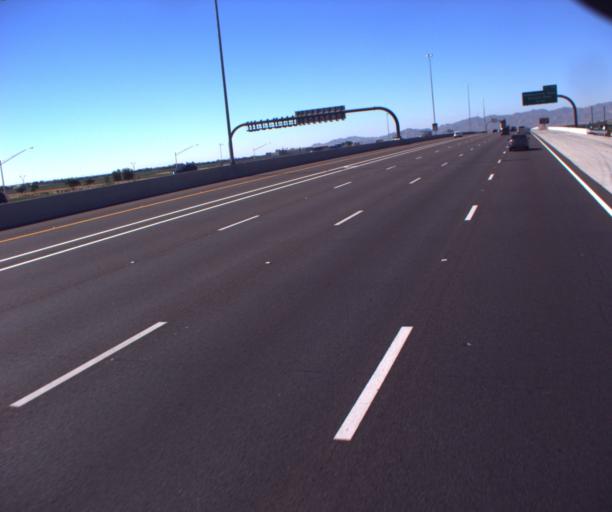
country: US
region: Arizona
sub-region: Maricopa County
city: Goodyear
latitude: 33.4594
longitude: -112.3719
